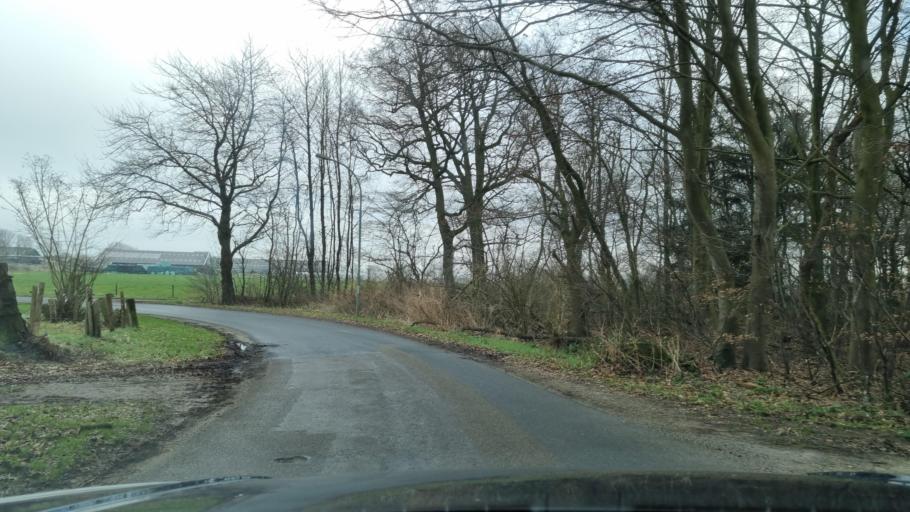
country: DE
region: North Rhine-Westphalia
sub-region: Regierungsbezirk Dusseldorf
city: Kleve
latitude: 51.7548
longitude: 6.1200
